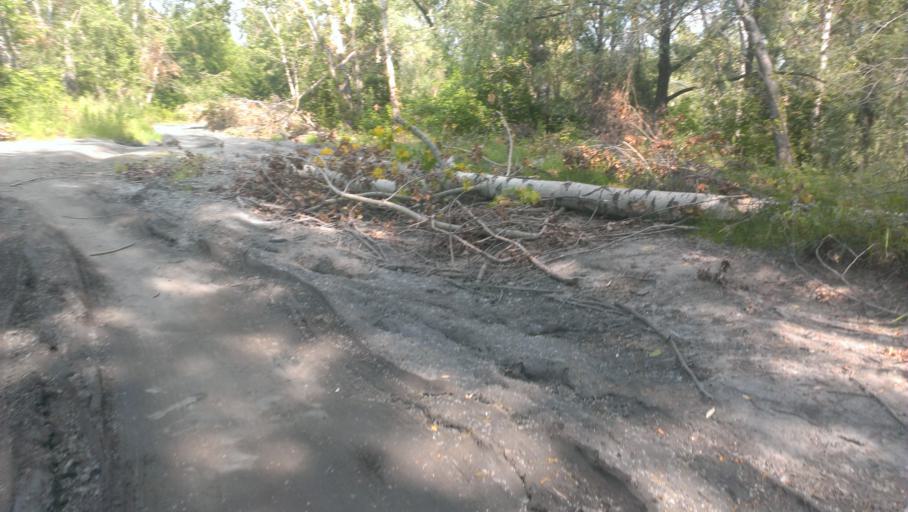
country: RU
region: Altai Krai
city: Novoaltaysk
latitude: 53.3709
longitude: 83.8551
